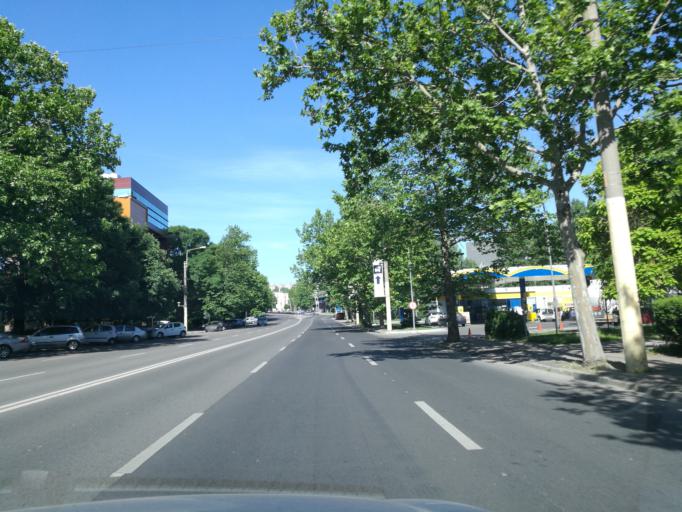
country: RO
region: Constanta
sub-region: Municipiul Constanta
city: Constanta
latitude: 44.2026
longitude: 28.6352
